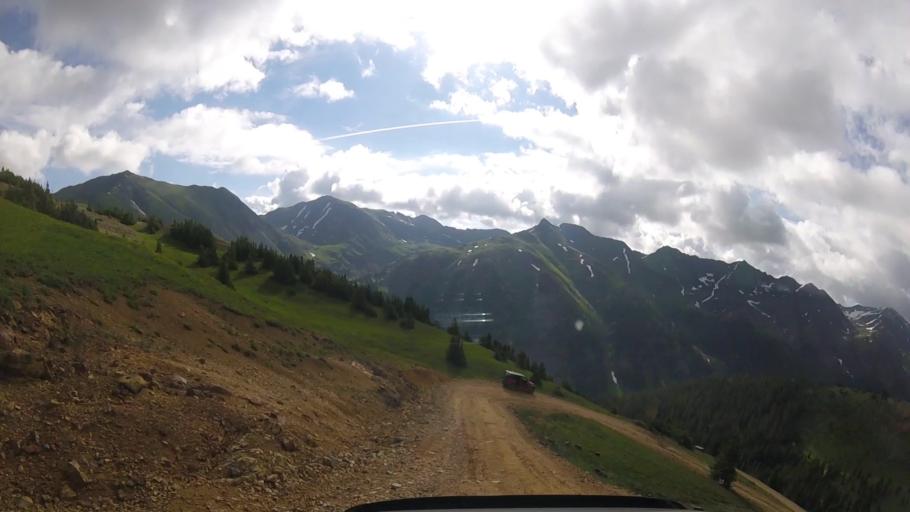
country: US
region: Colorado
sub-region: San Juan County
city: Silverton
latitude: 37.9062
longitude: -107.6583
